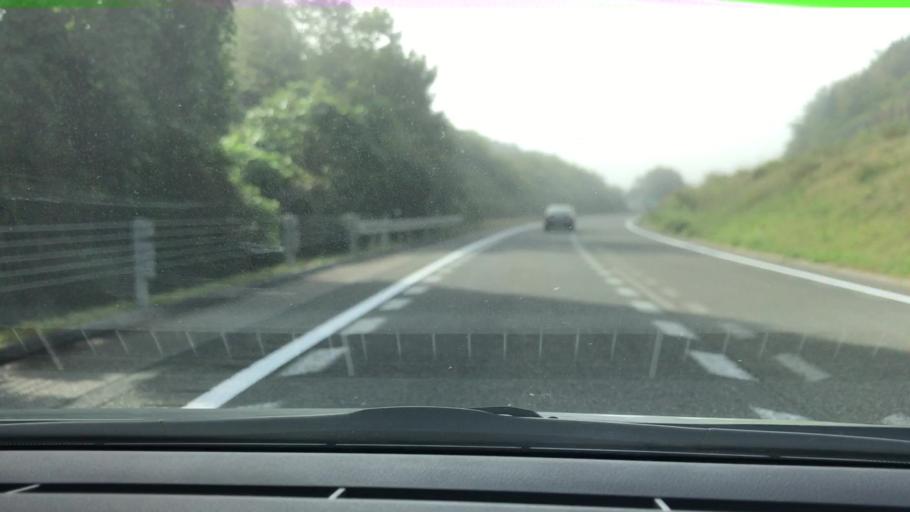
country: JP
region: Hyogo
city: Sasayama
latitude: 35.1045
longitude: 135.1707
